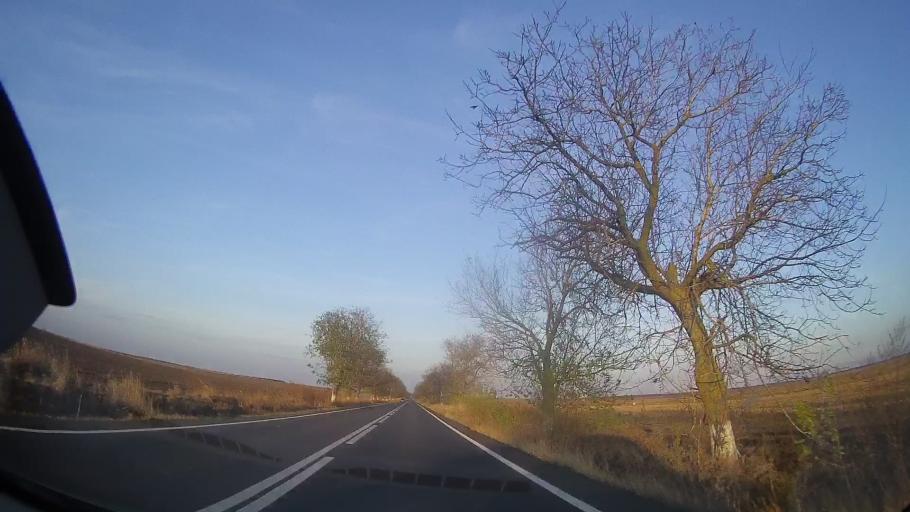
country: RO
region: Constanta
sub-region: Comuna Amzacea
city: Amzacea
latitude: 43.9396
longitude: 28.3697
